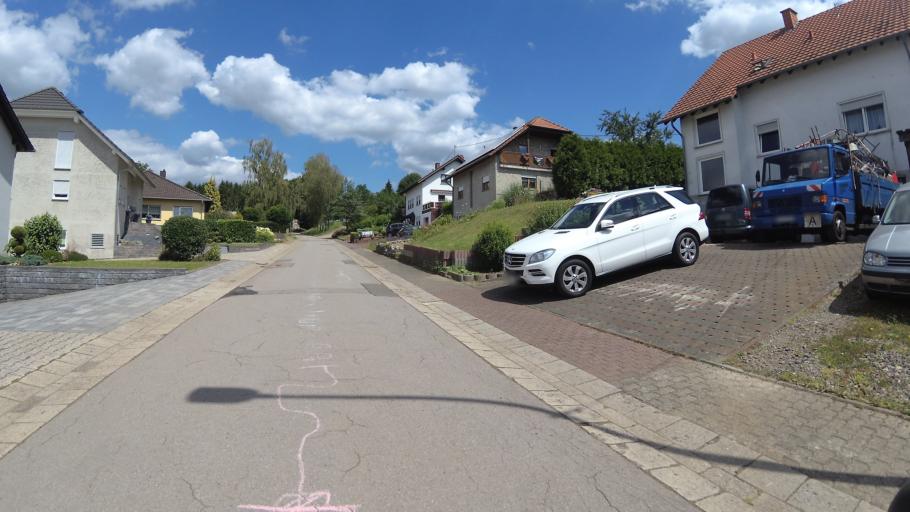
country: DE
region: Saarland
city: Wadern
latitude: 49.5305
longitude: 6.9248
